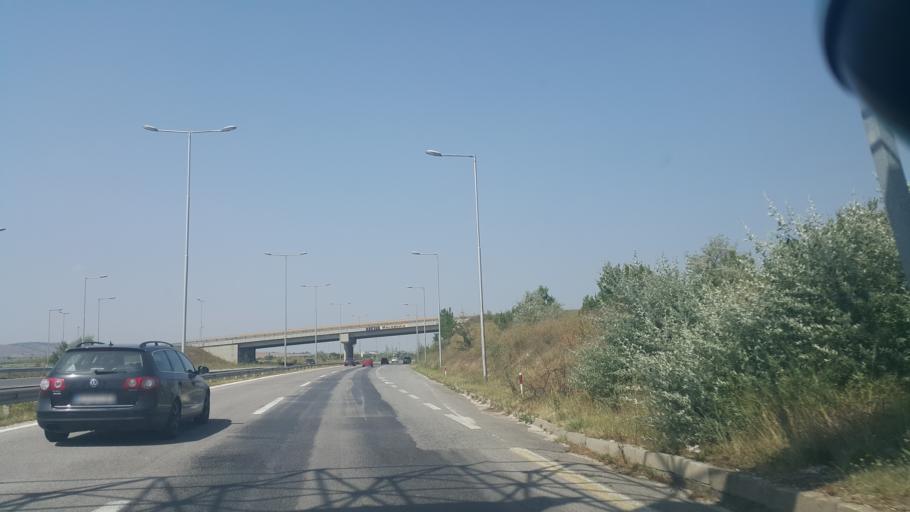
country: MK
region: Petrovec
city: Petrovec
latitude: 41.9576
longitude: 21.6315
